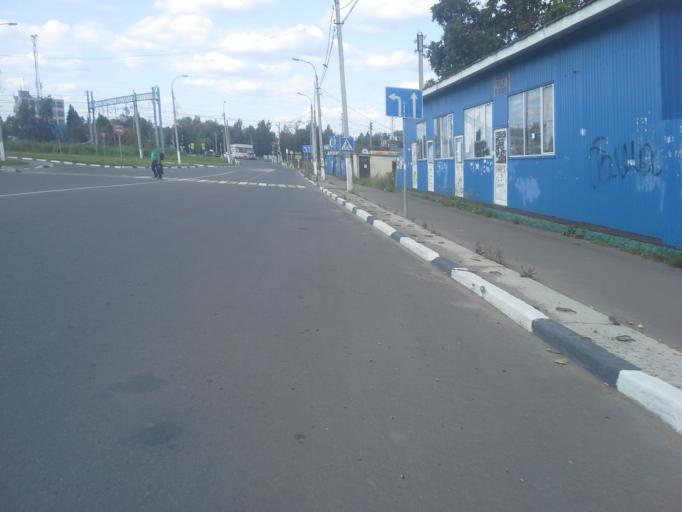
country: RU
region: Moskovskaya
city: Aprelevka
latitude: 55.5476
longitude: 37.0646
